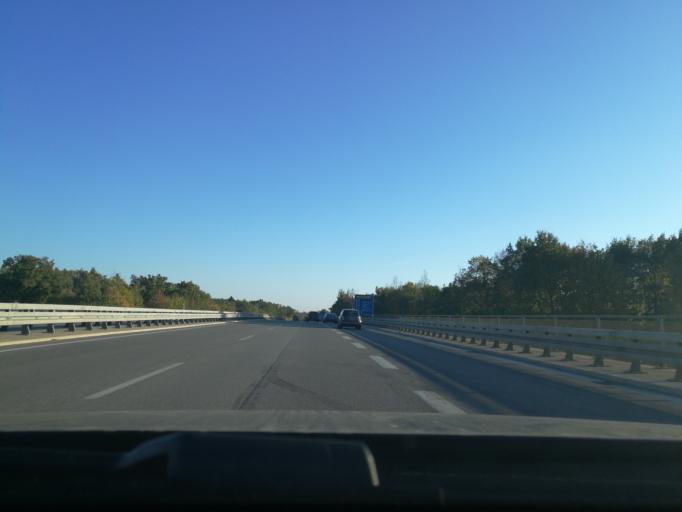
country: DE
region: Bavaria
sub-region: Regierungsbezirk Mittelfranken
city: Erlangen
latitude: 49.5388
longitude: 11.0304
